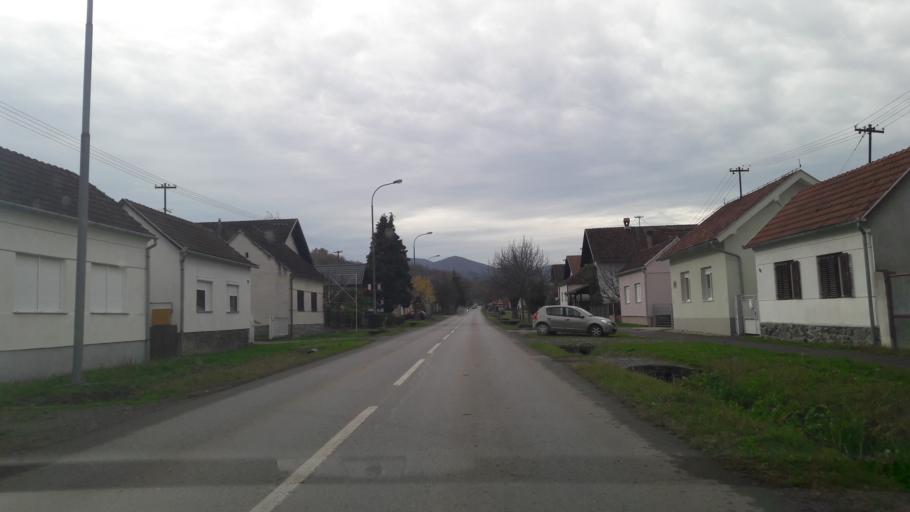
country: HR
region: Virovitick-Podravska
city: Orahovica
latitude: 45.5406
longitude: 17.8960
